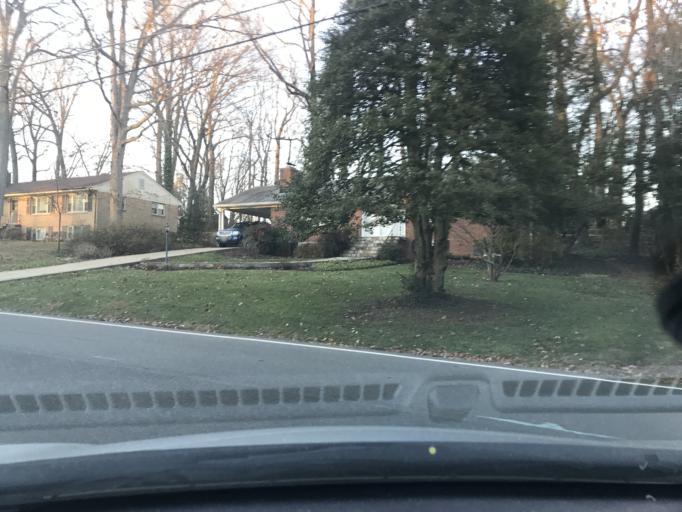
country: US
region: Virginia
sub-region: City of Fairfax
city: Fairfax
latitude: 38.8645
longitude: -77.3162
